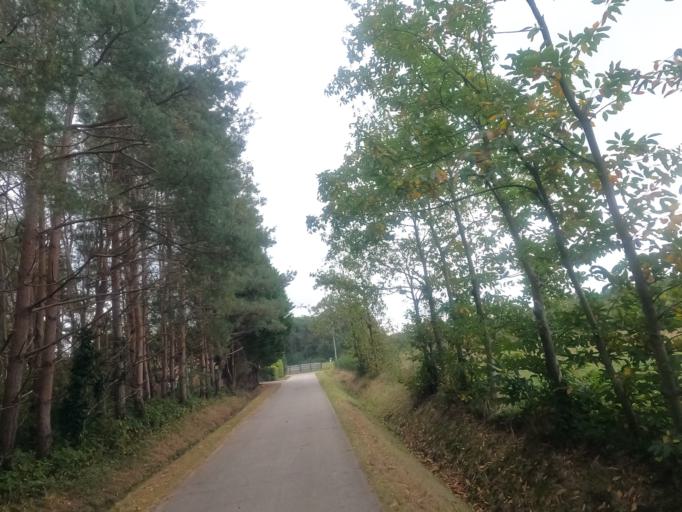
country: BE
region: Flanders
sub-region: Provincie Antwerpen
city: Nijlen
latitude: 51.1453
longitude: 4.6616
